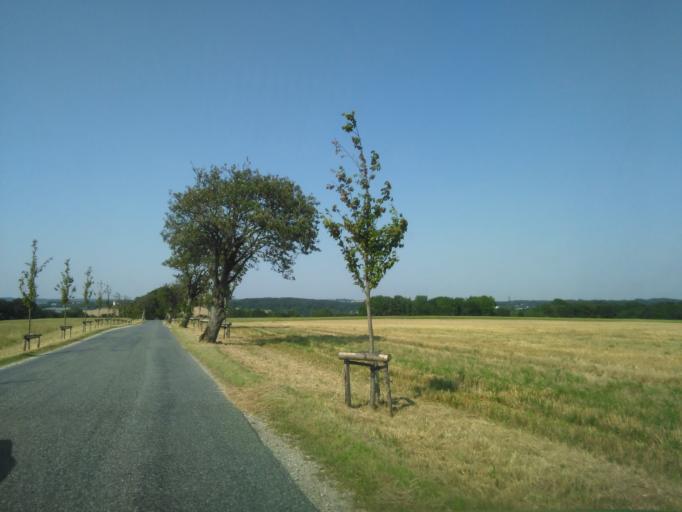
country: DK
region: Central Jutland
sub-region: Arhus Kommune
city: Kolt
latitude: 56.1329
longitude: 10.0785
